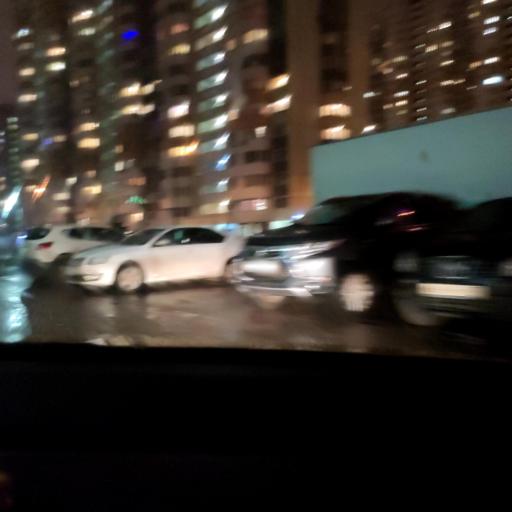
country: RU
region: Moskovskaya
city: Pavshino
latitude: 55.8418
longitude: 37.3786
